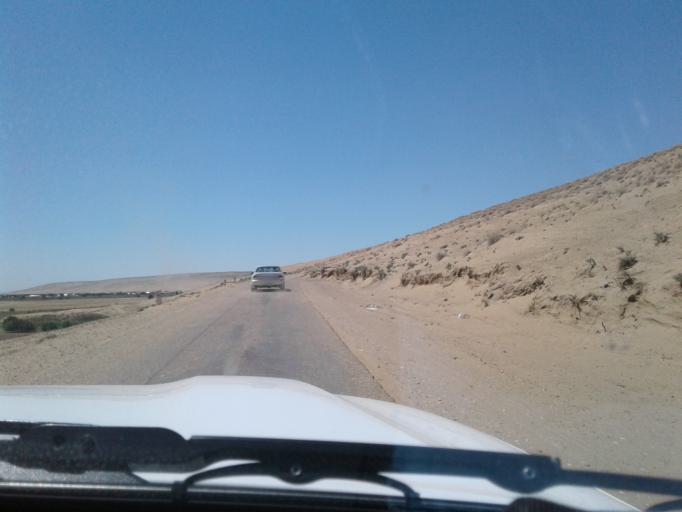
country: AF
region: Badghis
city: Bala Murghab
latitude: 35.9760
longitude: 62.9009
